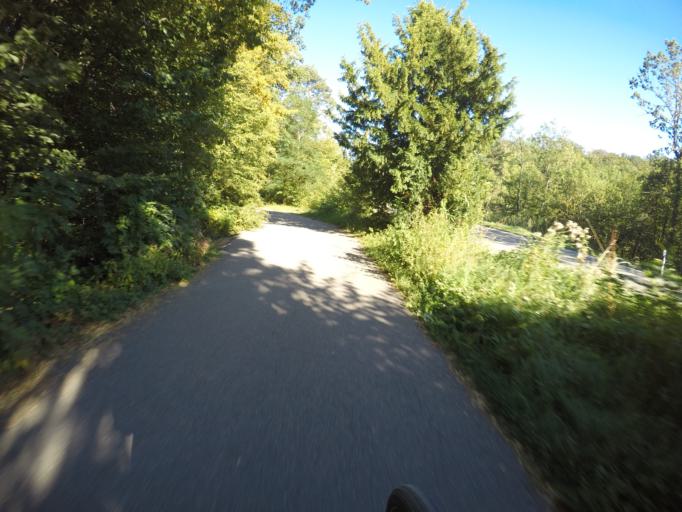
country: DE
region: Baden-Wuerttemberg
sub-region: Regierungsbezirk Stuttgart
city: Nufringen
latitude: 48.6028
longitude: 8.9007
